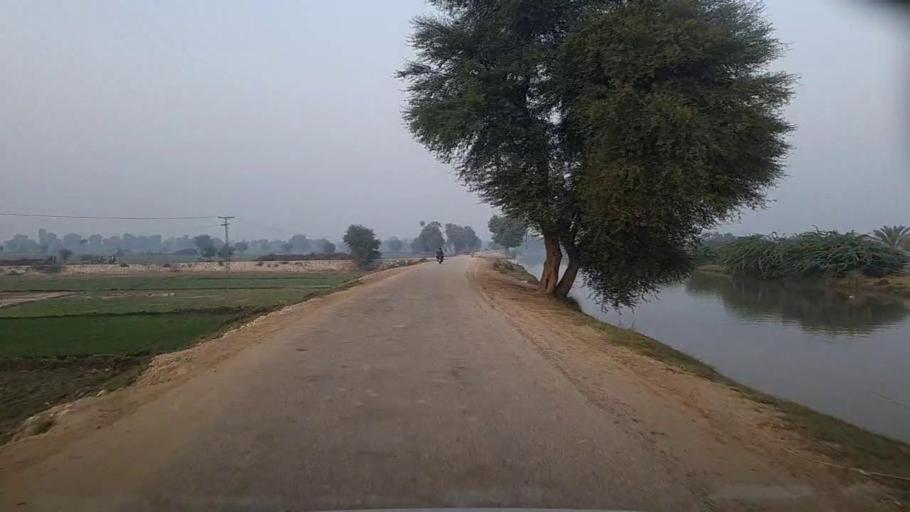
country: PK
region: Sindh
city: Bozdar
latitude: 27.0549
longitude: 68.5988
